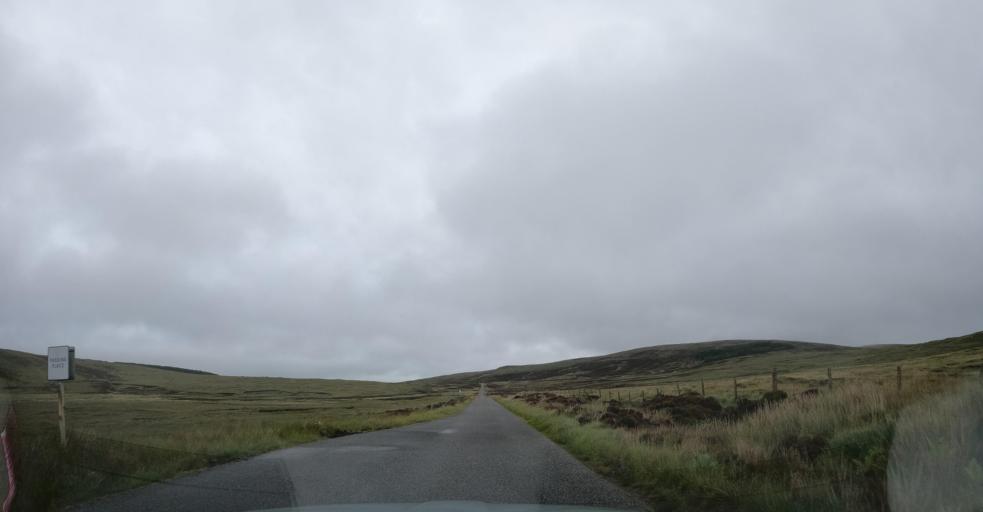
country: GB
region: Scotland
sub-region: Eilean Siar
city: Isle of North Uist
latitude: 57.6041
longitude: -7.3802
